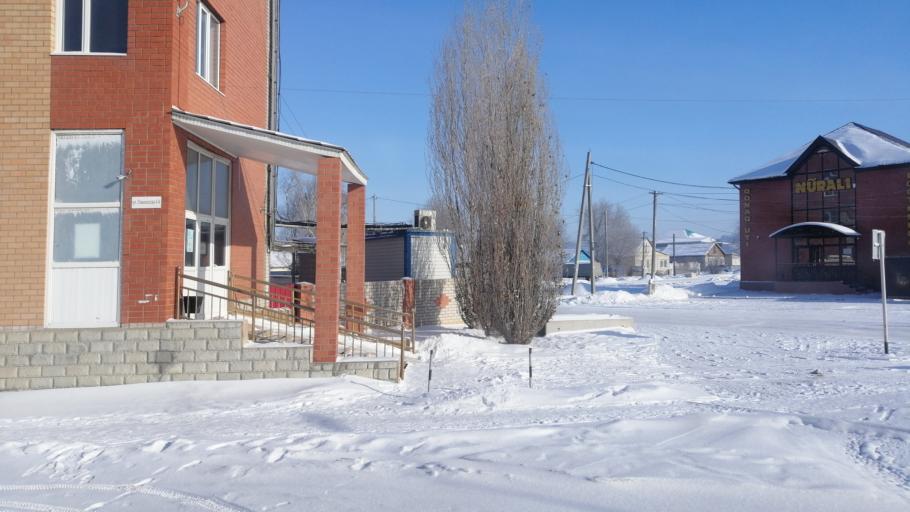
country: KZ
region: Aqtoebe
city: Aqtobe
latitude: 50.2873
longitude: 57.2066
